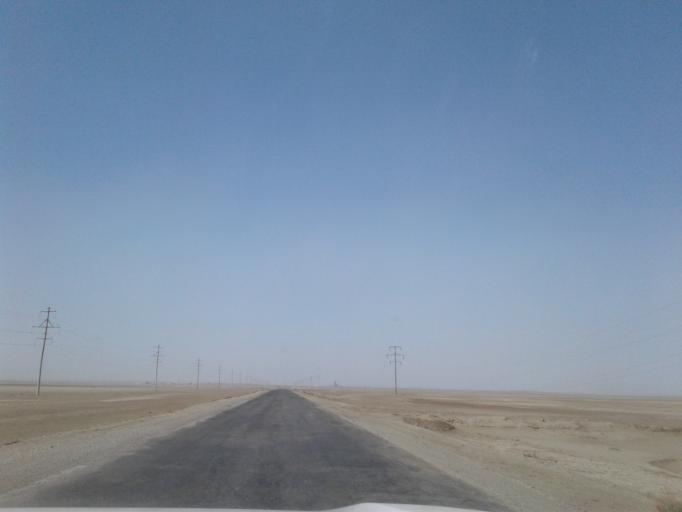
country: TM
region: Balkan
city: Gumdag
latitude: 39.0826
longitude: 54.5845
